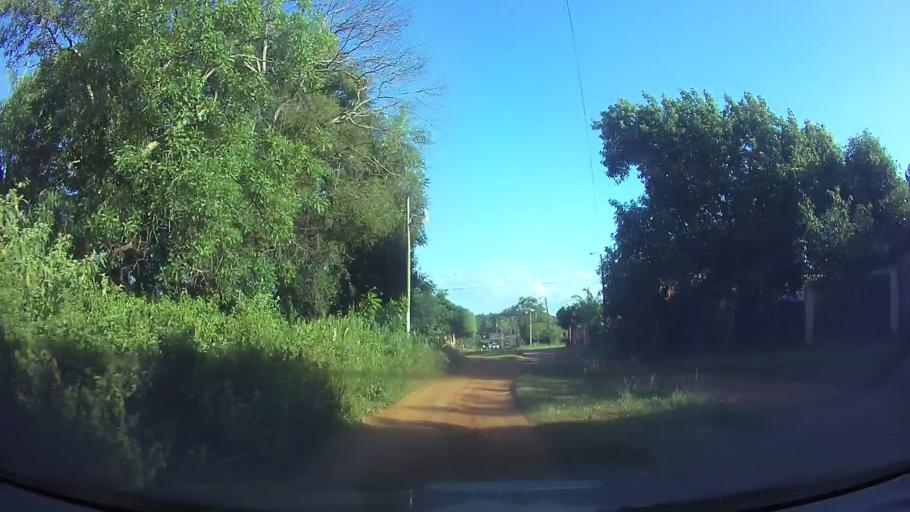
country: PY
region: Central
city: Limpio
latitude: -25.2561
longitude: -57.4685
